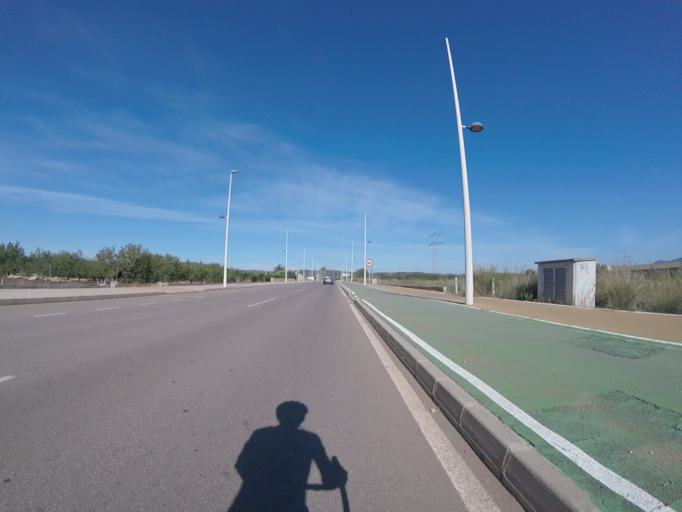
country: ES
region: Valencia
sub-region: Provincia de Castello
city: Torreblanca
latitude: 40.2156
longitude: 0.2212
